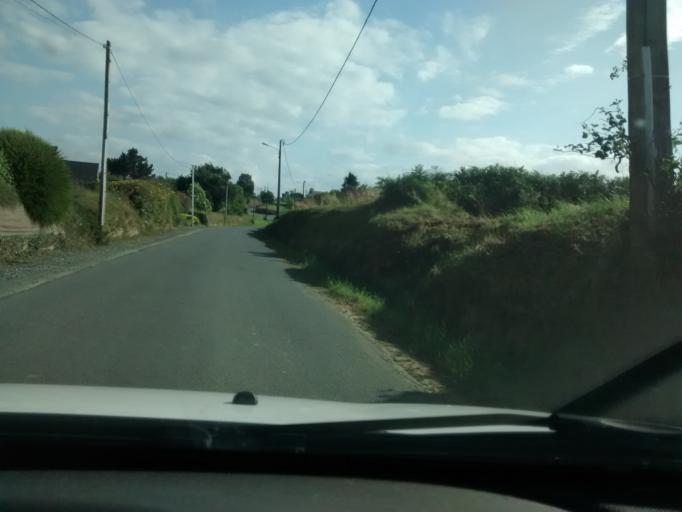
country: FR
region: Brittany
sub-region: Departement des Cotes-d'Armor
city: Penvenan
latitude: 48.8065
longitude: -3.2957
